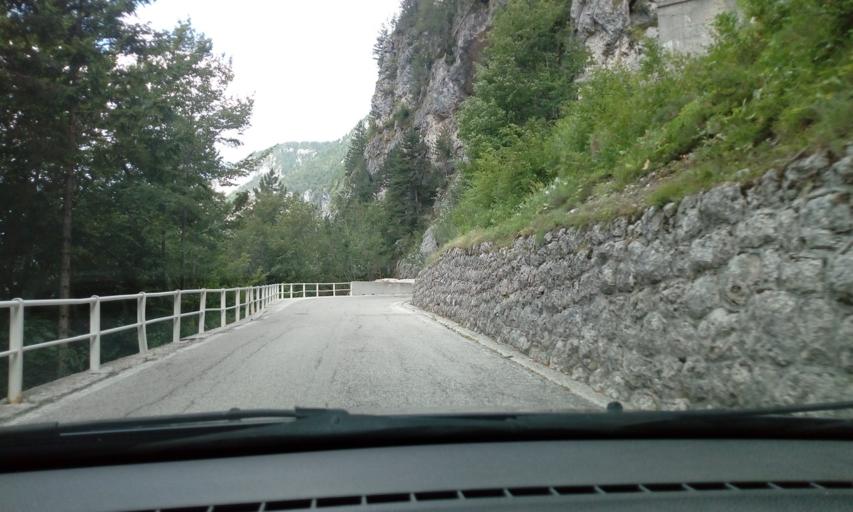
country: SI
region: Bovec
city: Bovec
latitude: 46.3933
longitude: 13.4619
